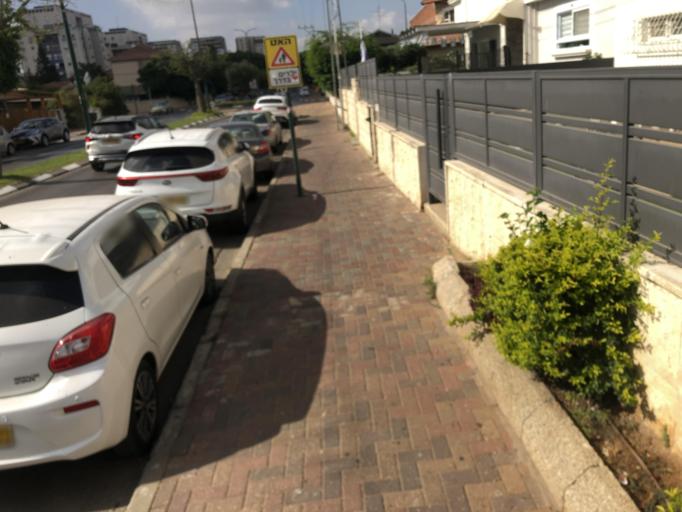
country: IL
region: Central District
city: Yehud
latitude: 32.0369
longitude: 34.8858
